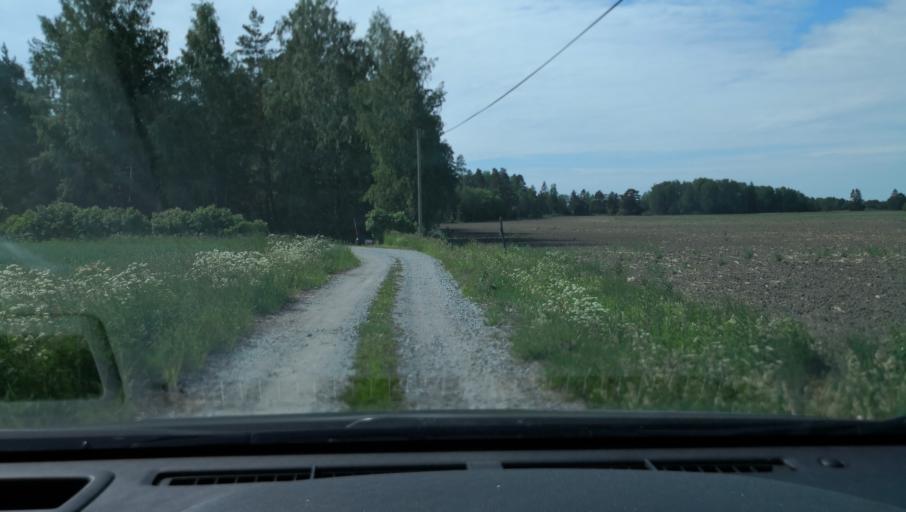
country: SE
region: Uppsala
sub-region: Enkopings Kommun
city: Enkoping
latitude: 59.7028
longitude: 17.1387
